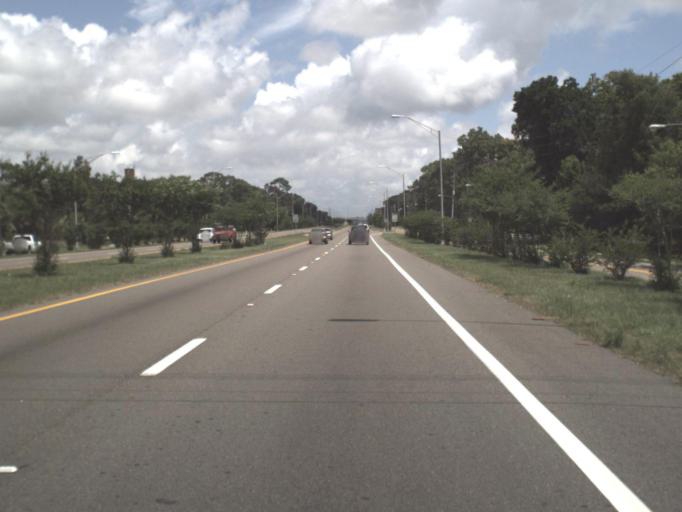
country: US
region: Florida
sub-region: Duval County
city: Jacksonville
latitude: 30.3019
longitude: -81.5586
